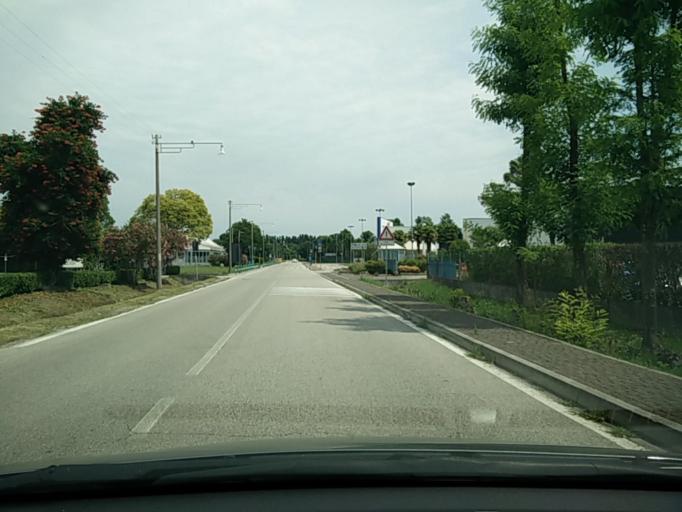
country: IT
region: Veneto
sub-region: Provincia di Venezia
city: San Liberale
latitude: 45.5198
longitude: 12.3575
